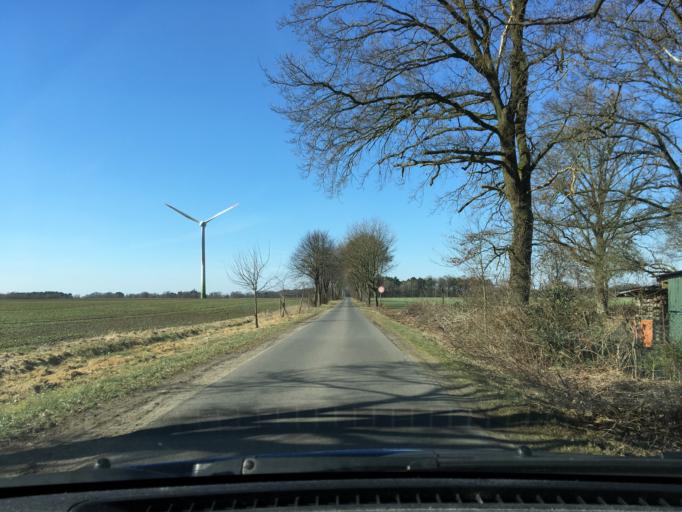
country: DE
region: Lower Saxony
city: Schneverdingen
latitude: 53.0826
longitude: 9.7864
